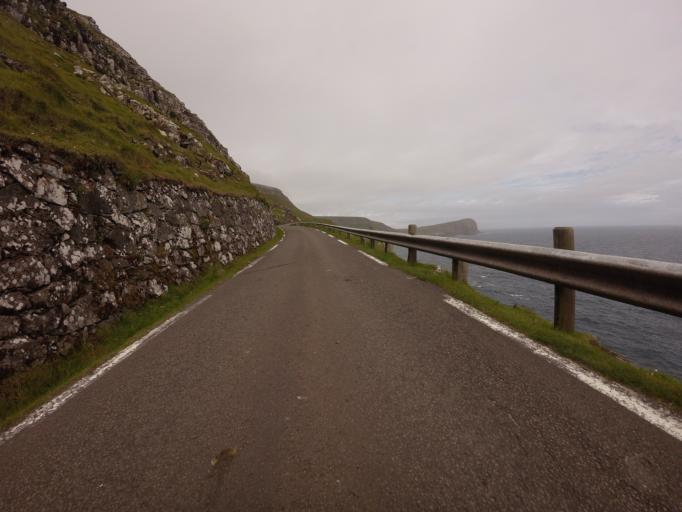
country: FO
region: Sandoy
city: Sandur
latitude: 61.7939
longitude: -6.6568
